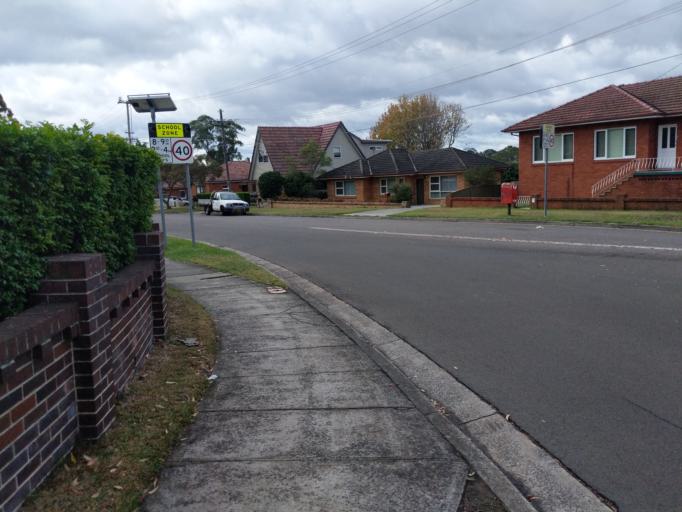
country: AU
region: New South Wales
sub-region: Kogarah
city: Hurstville Grove
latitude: -33.9779
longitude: 151.0829
